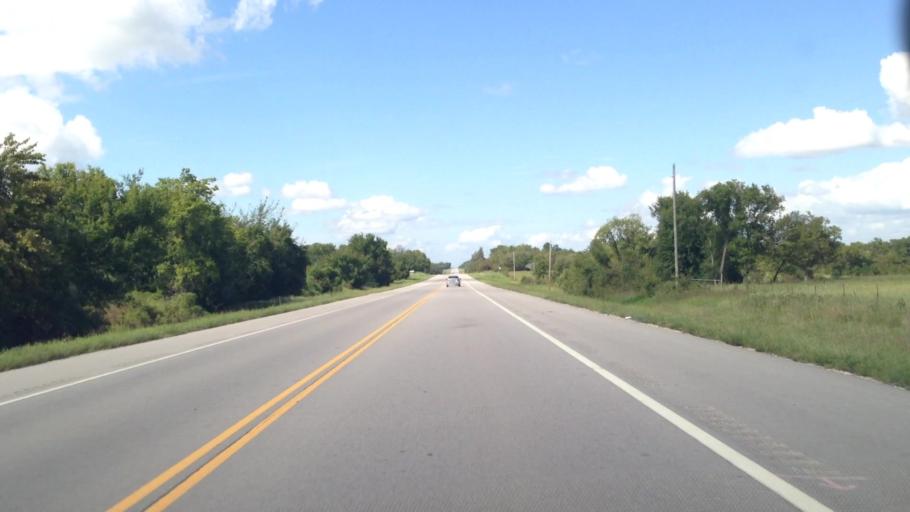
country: US
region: Kansas
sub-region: Labette County
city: Parsons
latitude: 37.2845
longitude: -95.2675
